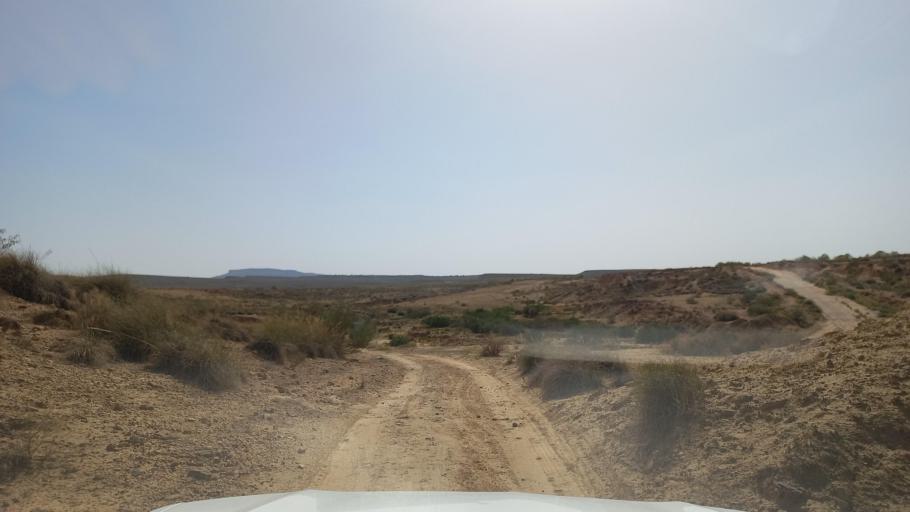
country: TN
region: Al Qasrayn
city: Kasserine
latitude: 35.2161
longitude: 9.0184
